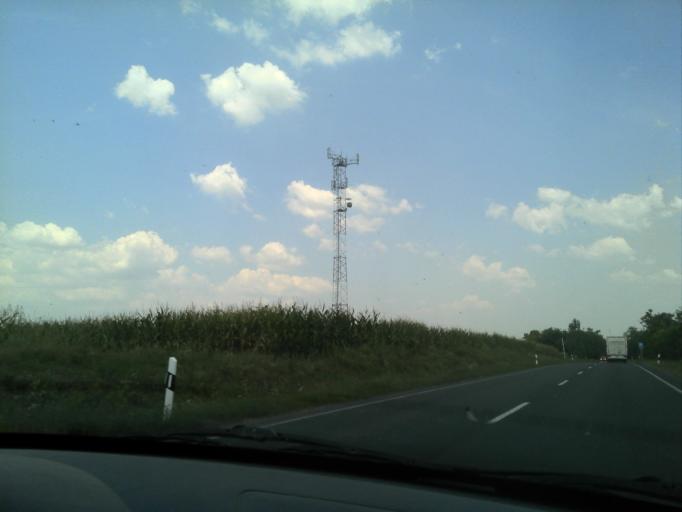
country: HU
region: Tolna
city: Iregszemcse
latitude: 46.5707
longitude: 18.1756
